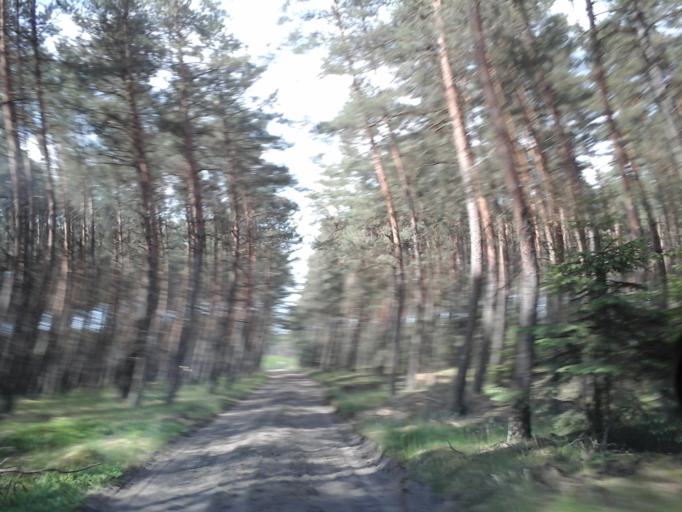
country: PL
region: West Pomeranian Voivodeship
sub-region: Powiat choszczenski
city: Drawno
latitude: 53.1435
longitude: 15.7652
